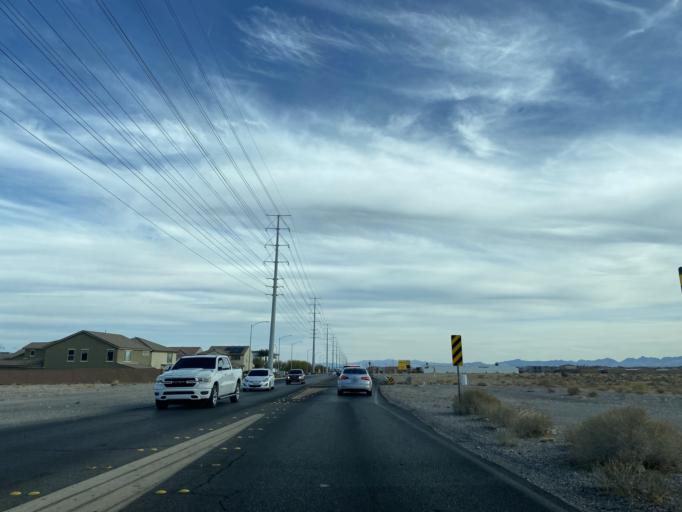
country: US
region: Nevada
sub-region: Clark County
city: Enterprise
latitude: 36.0555
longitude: -115.2676
